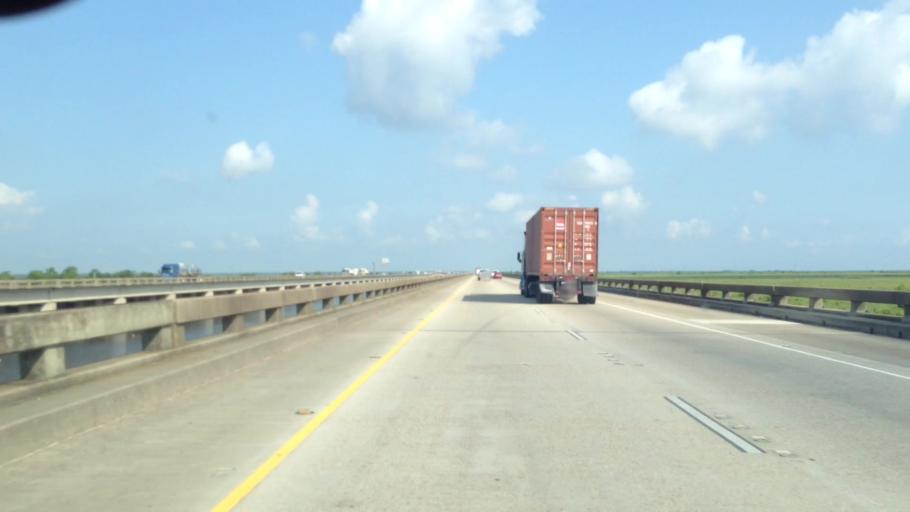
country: US
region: Louisiana
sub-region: Saint Charles Parish
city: Ama
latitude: 30.0213
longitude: -90.3208
